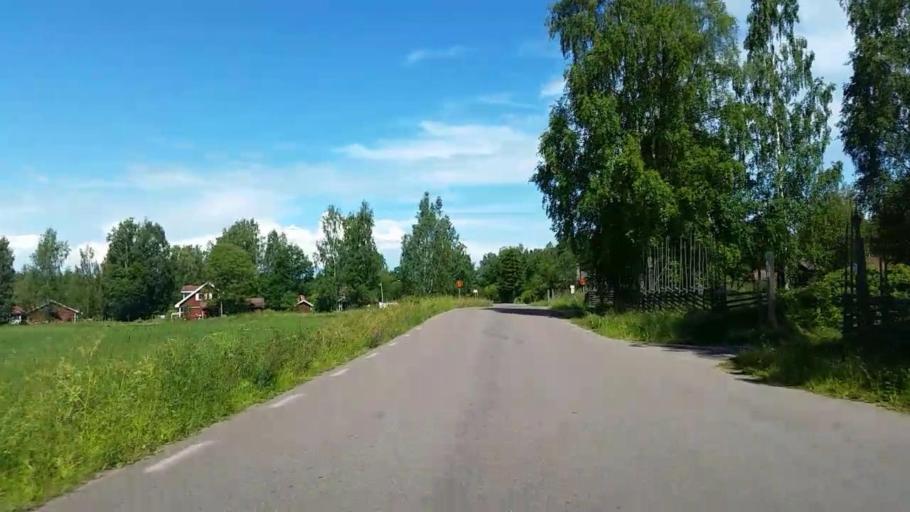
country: SE
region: Dalarna
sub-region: Rattviks Kommun
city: Vikarbyn
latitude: 60.8300
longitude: 14.9925
